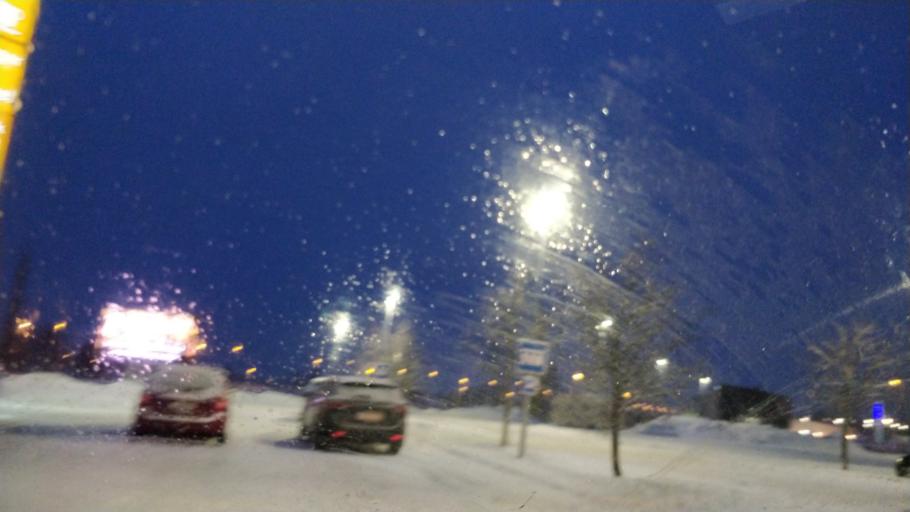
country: FI
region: Northern Ostrobothnia
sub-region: Oulu
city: Kempele
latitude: 64.8625
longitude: 25.5223
